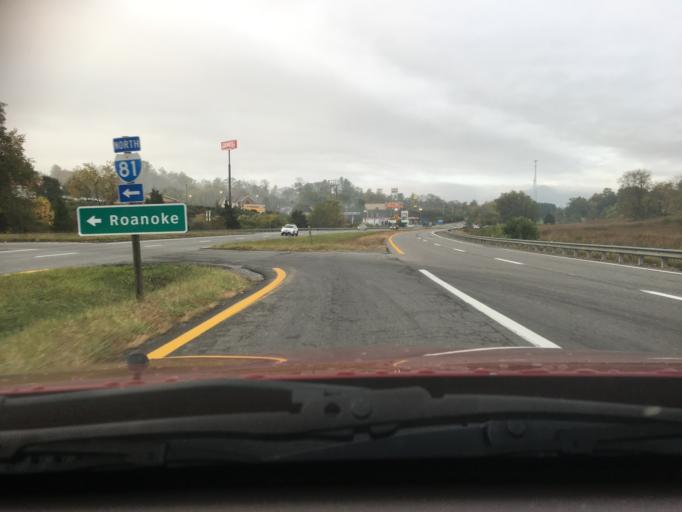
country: US
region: Virginia
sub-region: Pulaski County
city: Dublin
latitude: 37.0780
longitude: -80.6921
